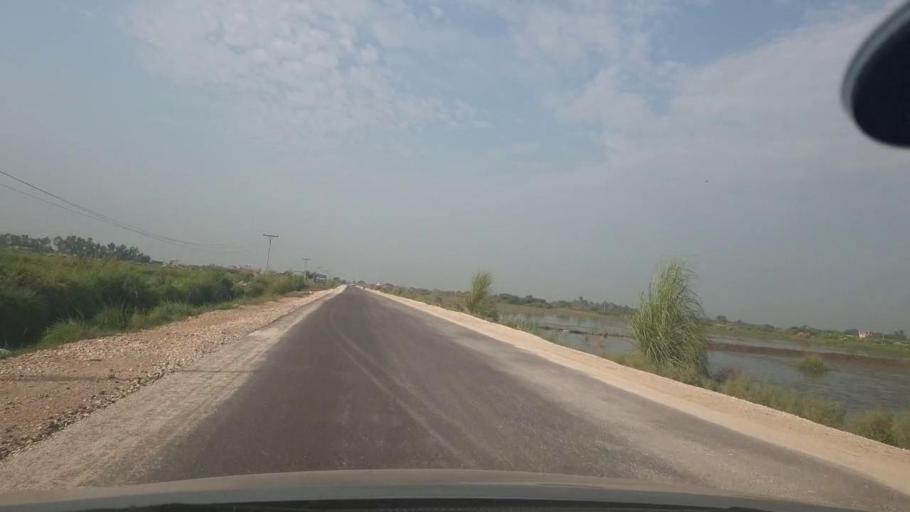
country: PK
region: Sindh
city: Jacobabad
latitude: 28.1429
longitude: 68.3438
